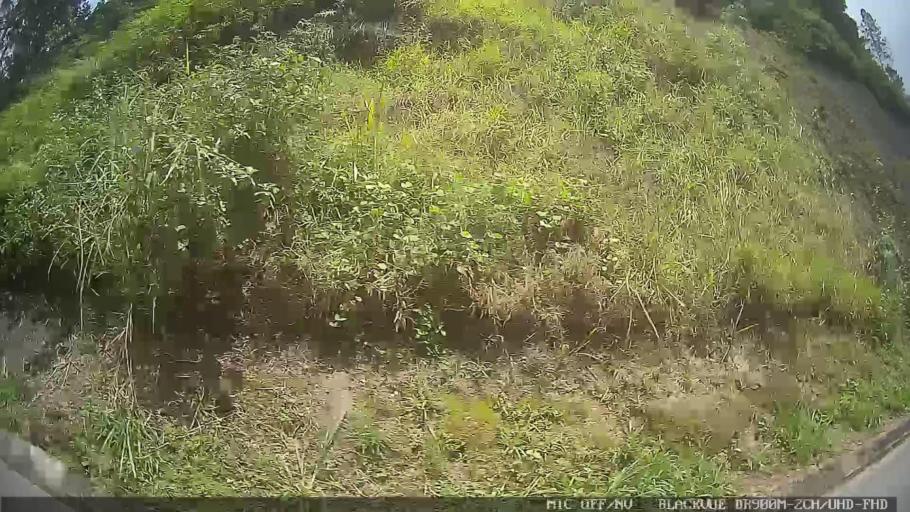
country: BR
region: Sao Paulo
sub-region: Caraguatatuba
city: Caraguatatuba
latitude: -23.5990
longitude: -45.4359
